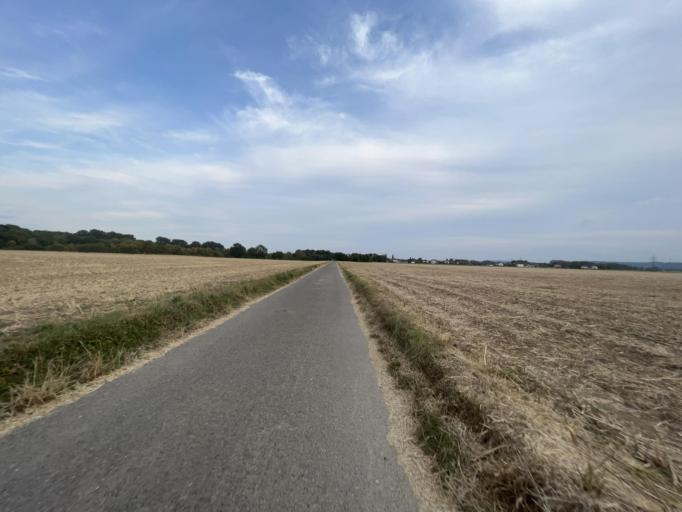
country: DE
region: North Rhine-Westphalia
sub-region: Regierungsbezirk Koln
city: Dueren
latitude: 50.8242
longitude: 6.4383
